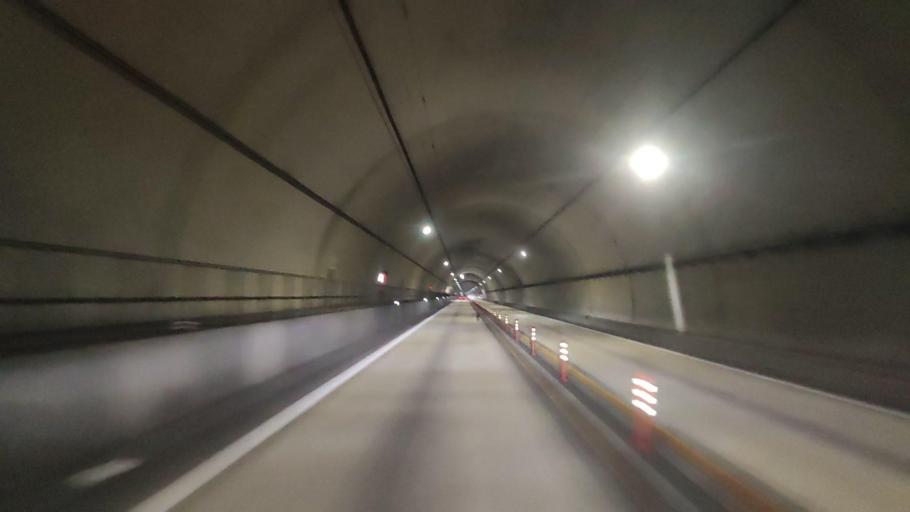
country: JP
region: Wakayama
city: Tanabe
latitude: 33.5686
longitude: 135.4879
